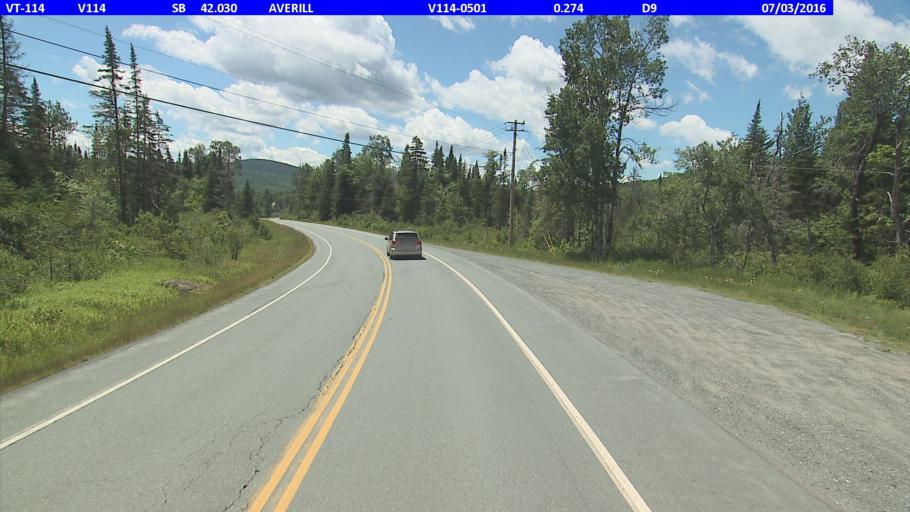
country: CA
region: Quebec
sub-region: Estrie
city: Coaticook
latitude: 45.0025
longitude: -71.7048
